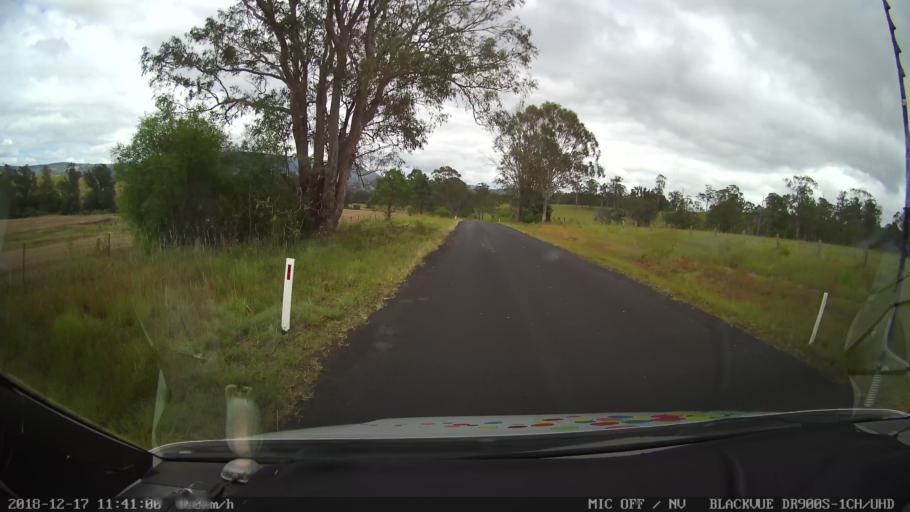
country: AU
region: New South Wales
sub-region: Kyogle
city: Kyogle
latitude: -28.6778
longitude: 152.5912
